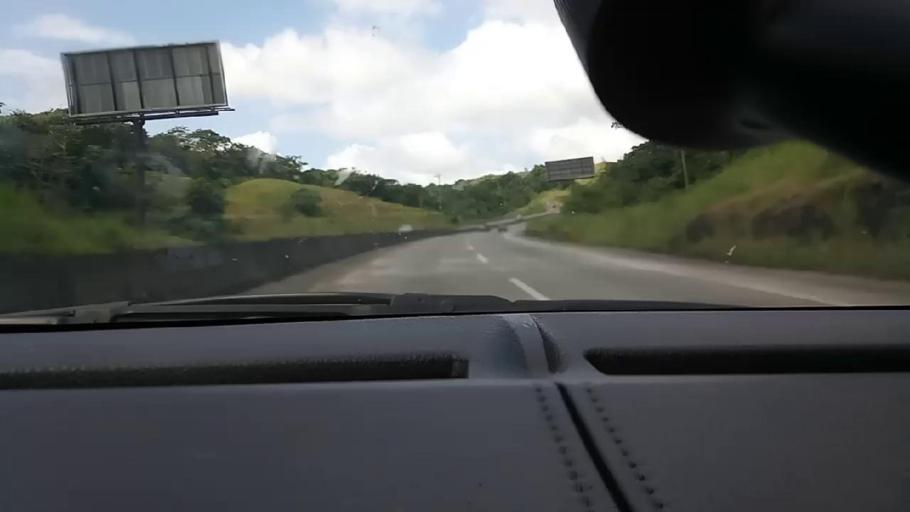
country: PA
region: Colon
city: Gatun
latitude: 9.2831
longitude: -79.7752
